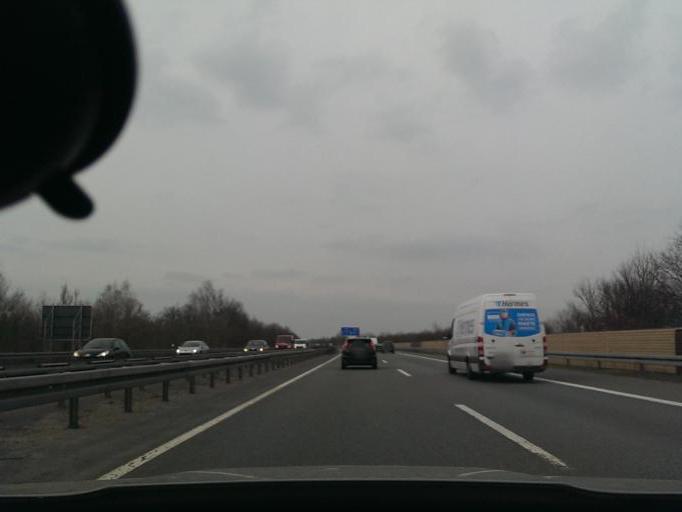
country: DE
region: North Rhine-Westphalia
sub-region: Regierungsbezirk Detmold
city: Hovelhof
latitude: 51.7780
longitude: 8.7023
